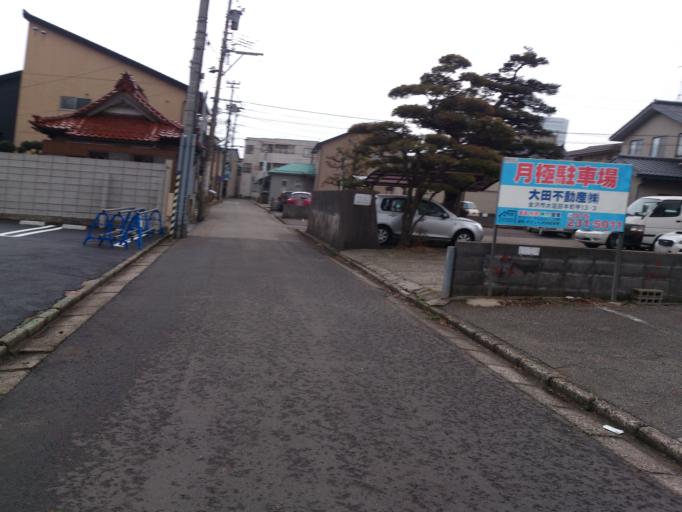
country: JP
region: Ishikawa
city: Kanazawa-shi
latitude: 36.5680
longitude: 136.6452
